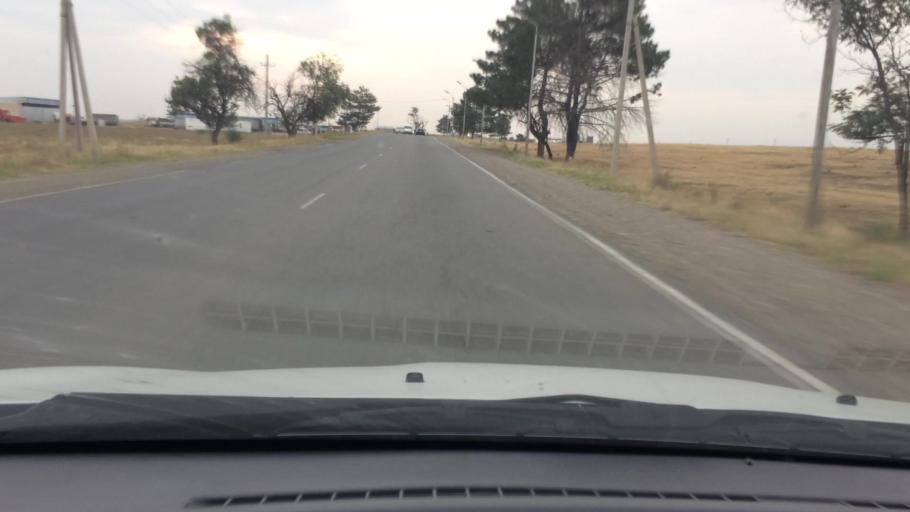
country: GE
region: Kvemo Kartli
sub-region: Marneuli
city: Marneuli
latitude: 41.5146
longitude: 44.7872
